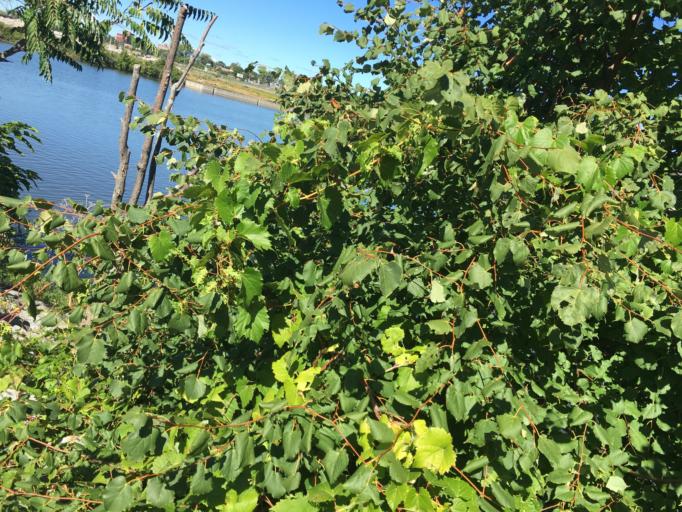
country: US
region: New York
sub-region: Onondaga County
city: Syracuse
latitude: 43.0601
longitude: -76.1659
